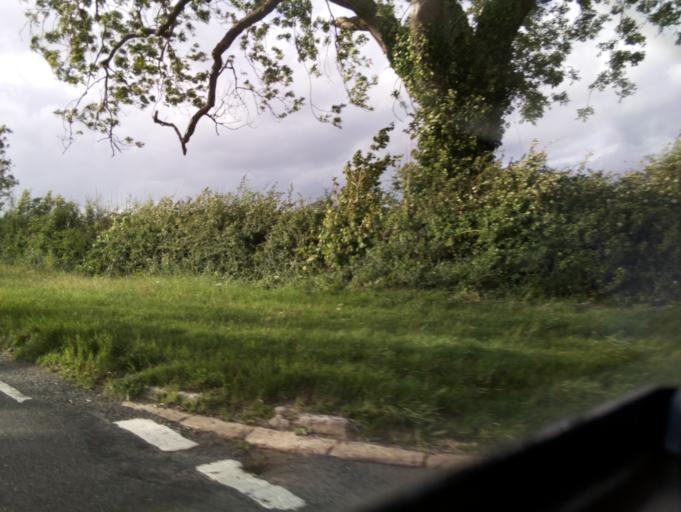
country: GB
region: England
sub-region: Gloucestershire
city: Donnington
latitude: 51.9462
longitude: -1.7339
